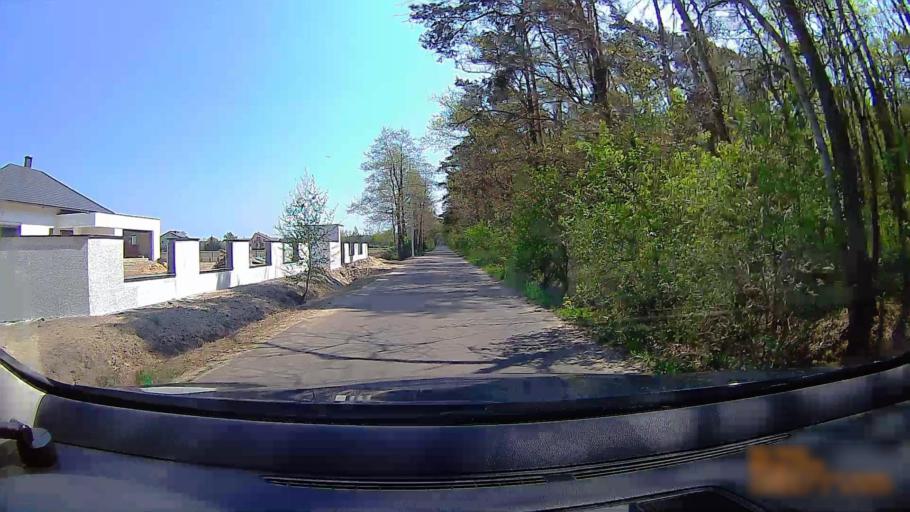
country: PL
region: Greater Poland Voivodeship
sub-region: Powiat koninski
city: Rychwal
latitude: 52.0940
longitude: 18.1704
